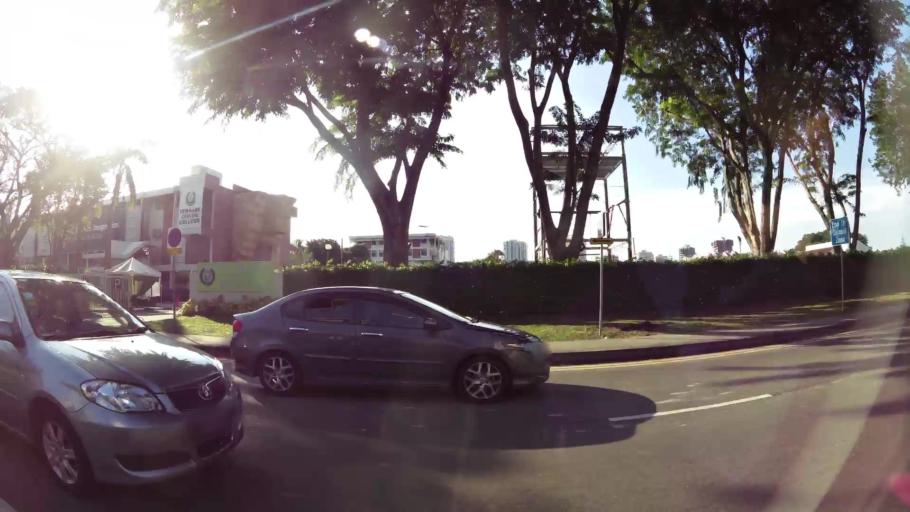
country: SG
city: Singapore
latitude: 1.3194
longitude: 103.9347
